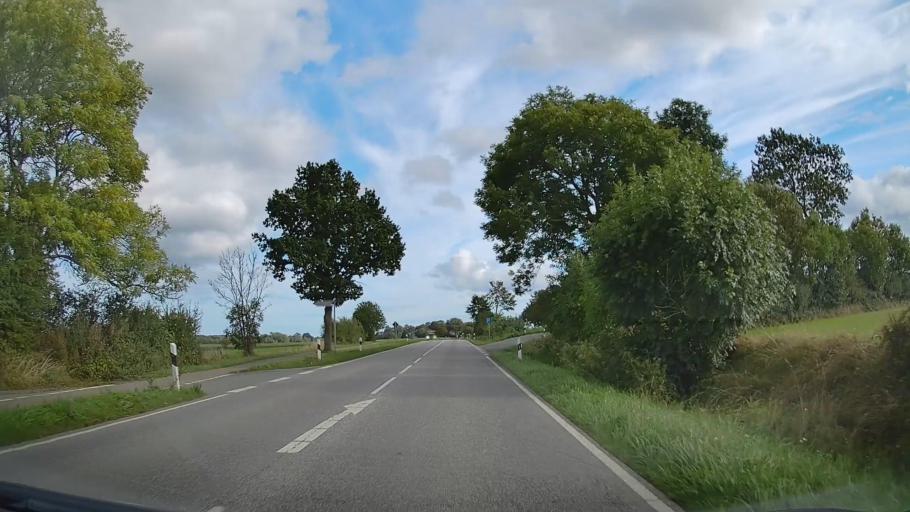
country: DE
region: Schleswig-Holstein
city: Stangheck
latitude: 54.7490
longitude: 9.8584
